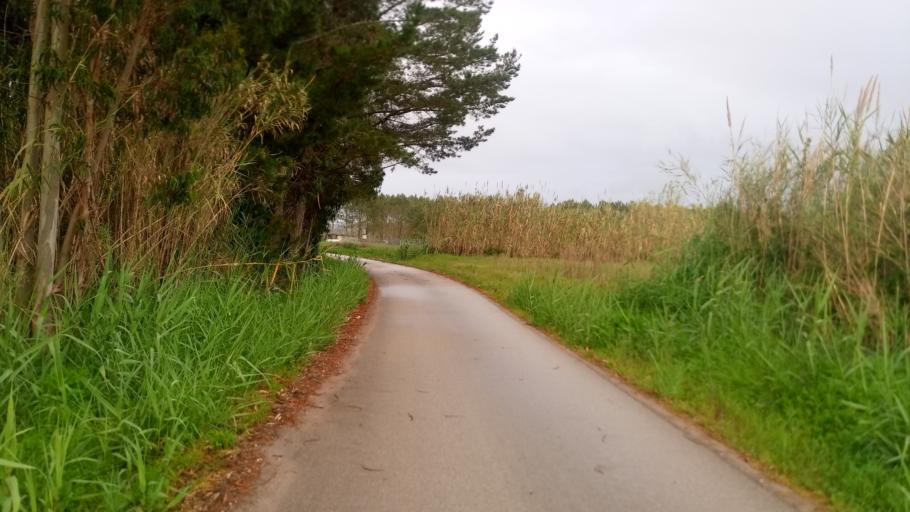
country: PT
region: Leiria
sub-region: Caldas da Rainha
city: Caldas da Rainha
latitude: 39.4364
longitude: -9.1626
